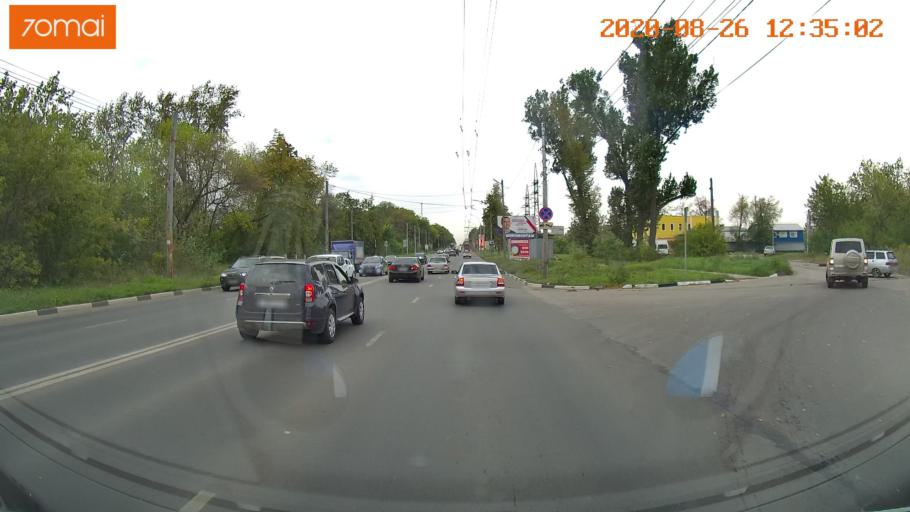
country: RU
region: Rjazan
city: Ryazan'
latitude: 54.5926
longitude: 39.7695
